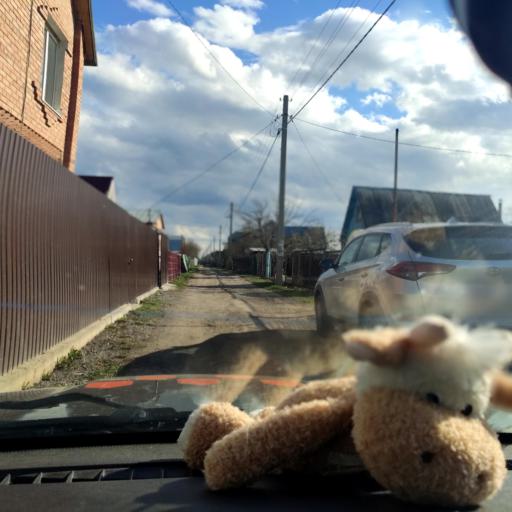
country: RU
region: Samara
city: Tol'yatti
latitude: 53.5978
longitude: 49.3094
